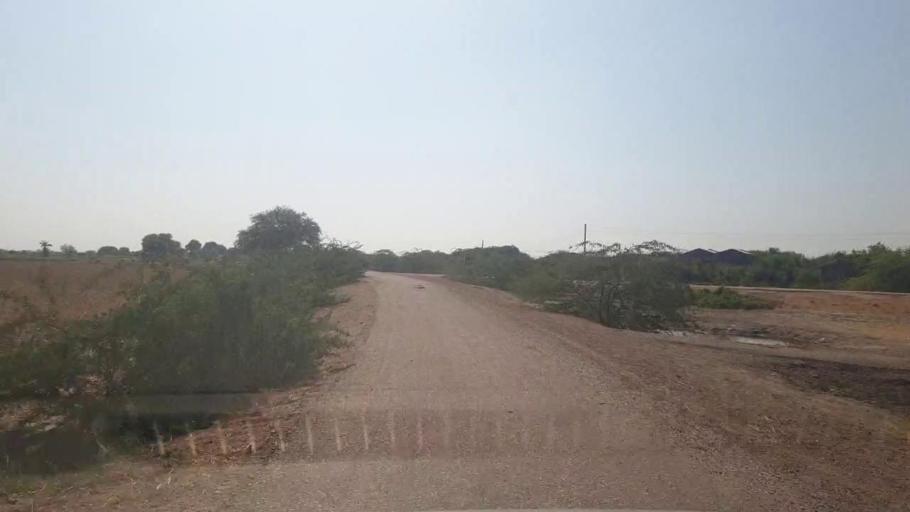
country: PK
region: Sindh
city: Badin
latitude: 24.5535
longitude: 68.8149
